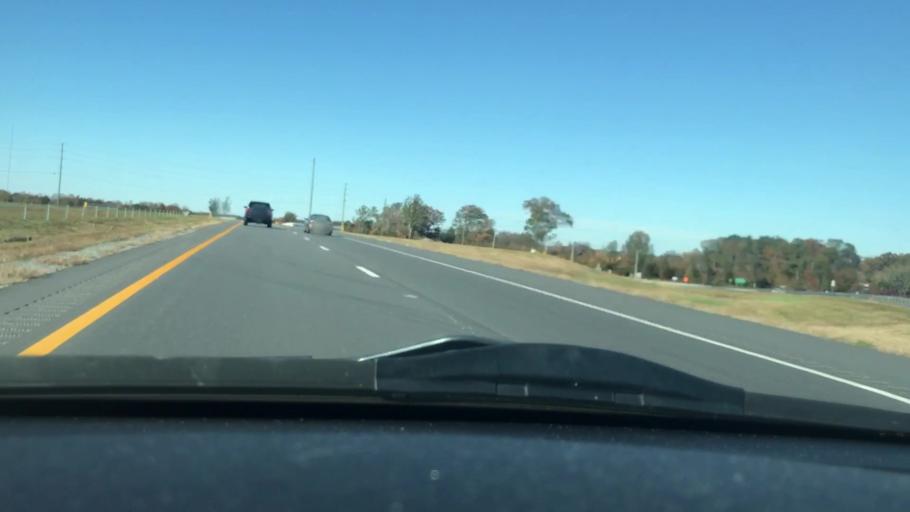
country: US
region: North Carolina
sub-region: Guilford County
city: Summerfield
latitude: 36.2450
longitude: -79.9201
